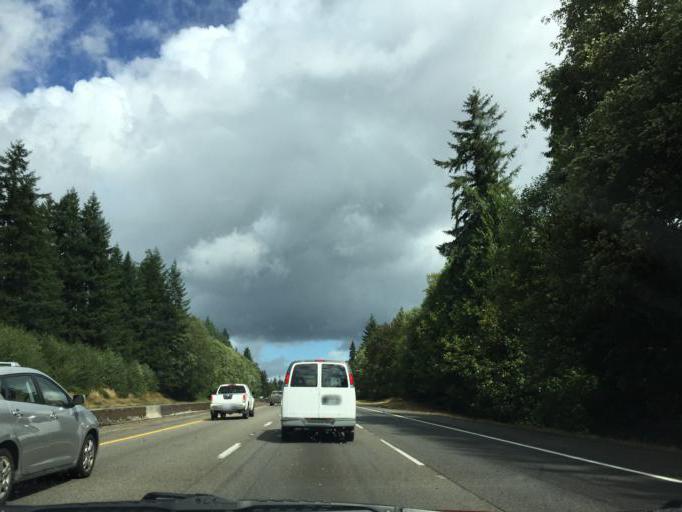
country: US
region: Washington
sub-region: Lewis County
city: Winlock
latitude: 46.4840
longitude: -122.8800
